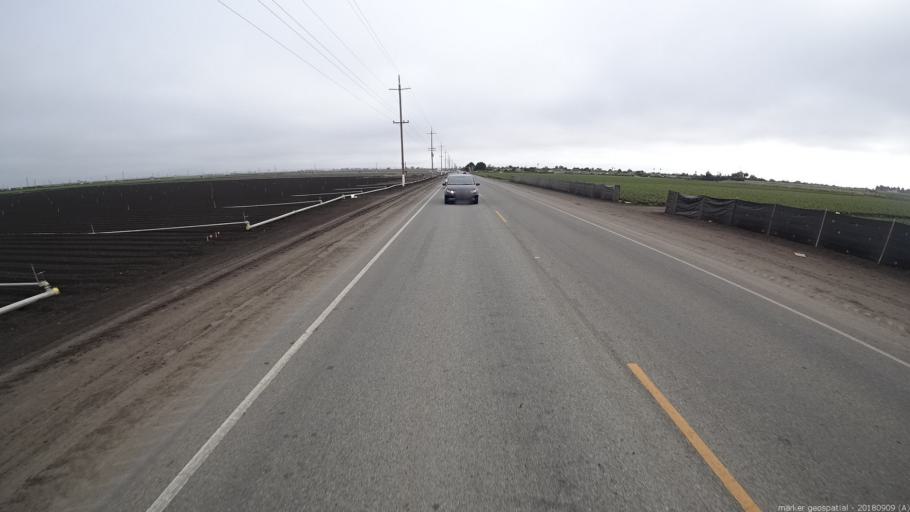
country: US
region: California
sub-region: Monterey County
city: Salinas
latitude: 36.6632
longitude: -121.6880
